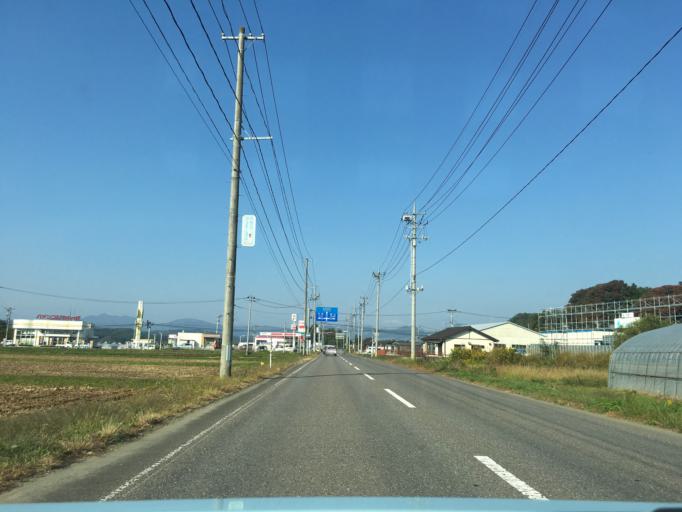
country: JP
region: Fukushima
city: Sukagawa
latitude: 37.2794
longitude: 140.2745
